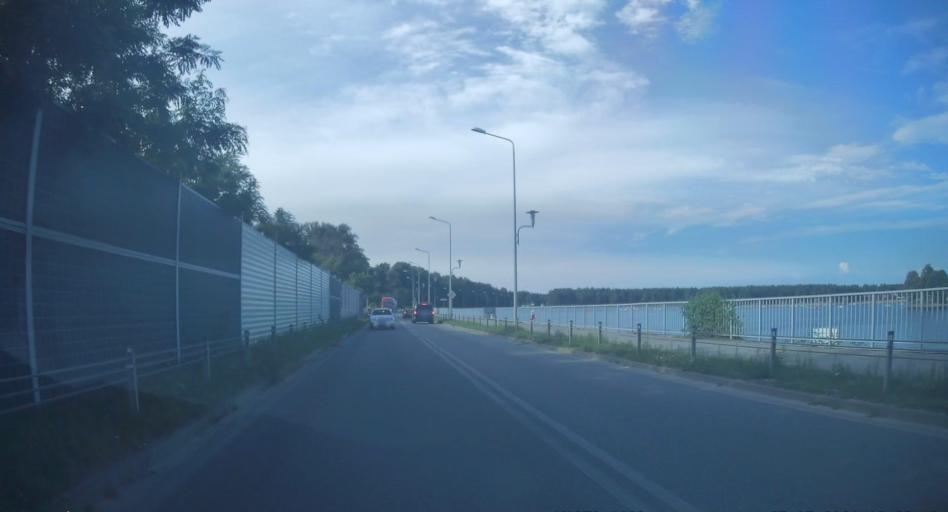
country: PL
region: Swietokrzyskie
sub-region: Powiat konecki
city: Smykow
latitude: 51.1128
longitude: 20.3494
